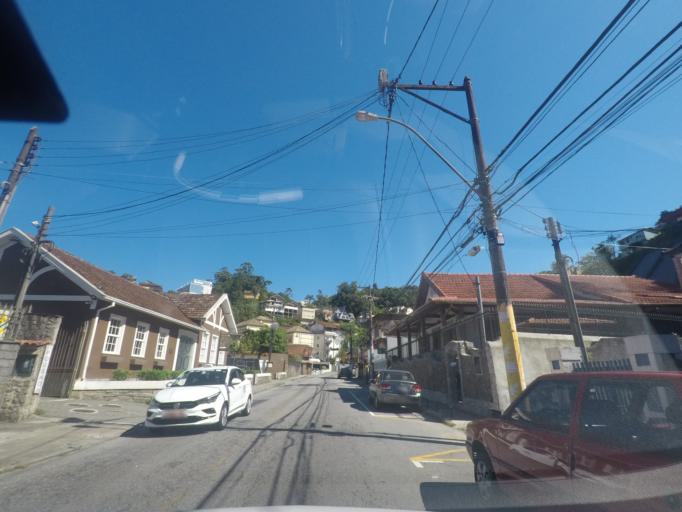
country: BR
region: Rio de Janeiro
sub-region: Petropolis
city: Petropolis
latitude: -22.5182
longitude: -43.1913
